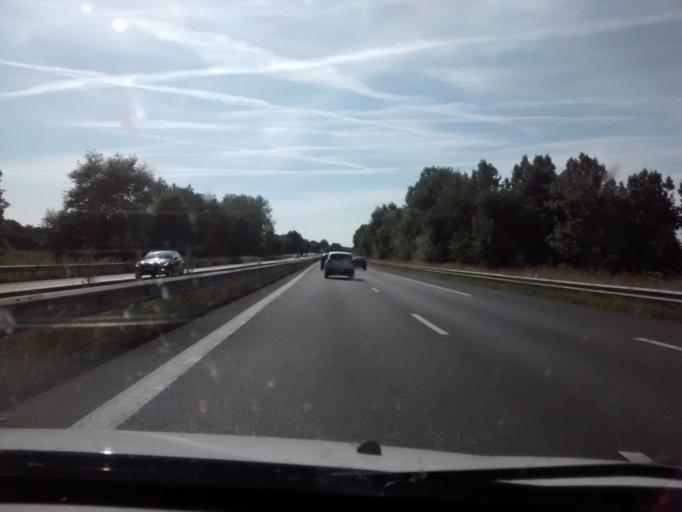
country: FR
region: Brittany
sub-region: Departement d'Ille-et-Vilaine
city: Saint-Didier
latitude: 48.0920
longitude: -1.3881
